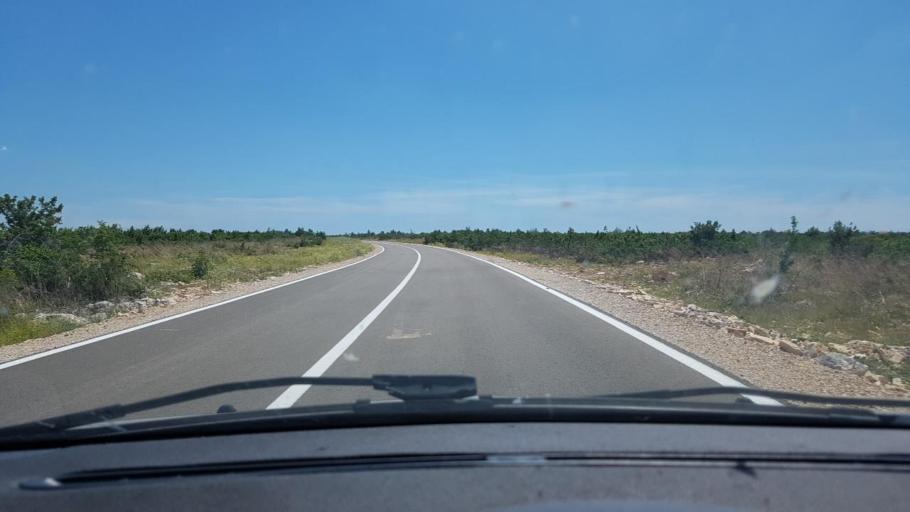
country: HR
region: Sibensko-Kniniska
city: Kistanje
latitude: 43.9297
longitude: 15.9346
